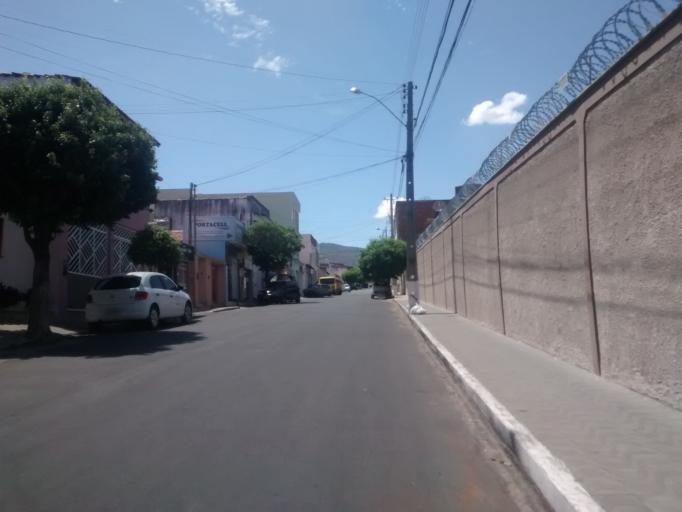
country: BR
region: Bahia
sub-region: Brumado
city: Brumado
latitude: -14.2091
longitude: -41.6714
